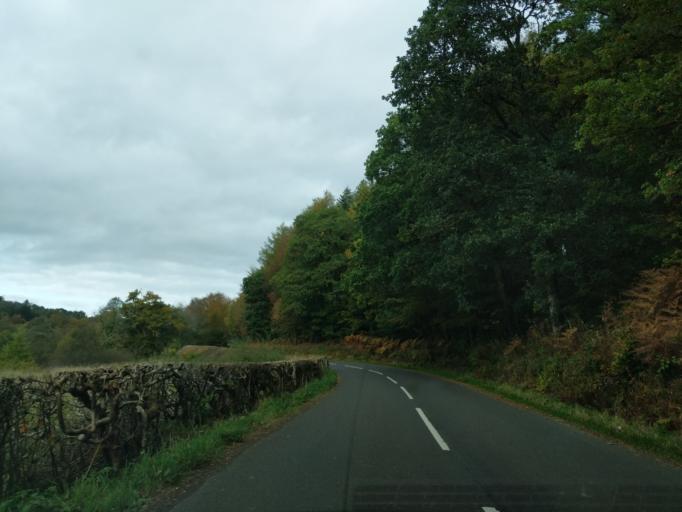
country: GB
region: Scotland
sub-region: Dumfries and Galloway
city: Thornhill
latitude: 55.2671
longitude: -3.7787
